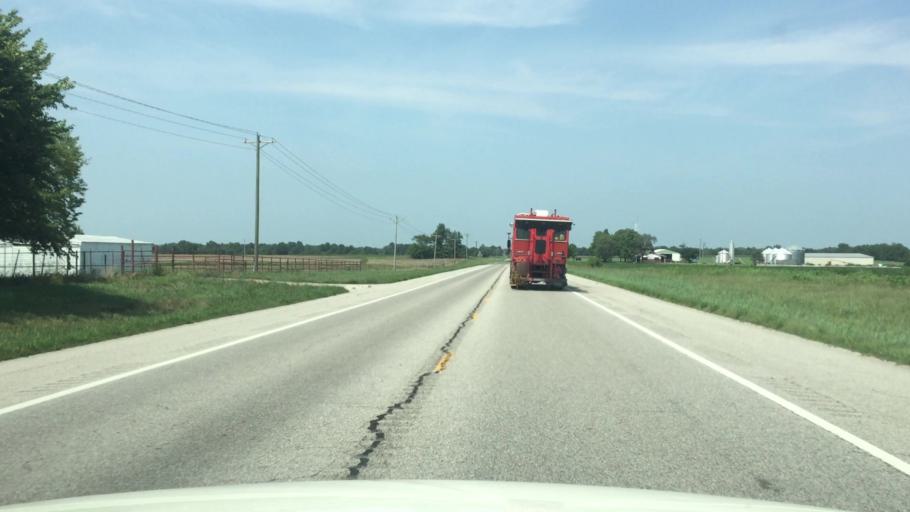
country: US
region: Missouri
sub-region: Jasper County
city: Carl Junction
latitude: 37.2332
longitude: -94.7049
